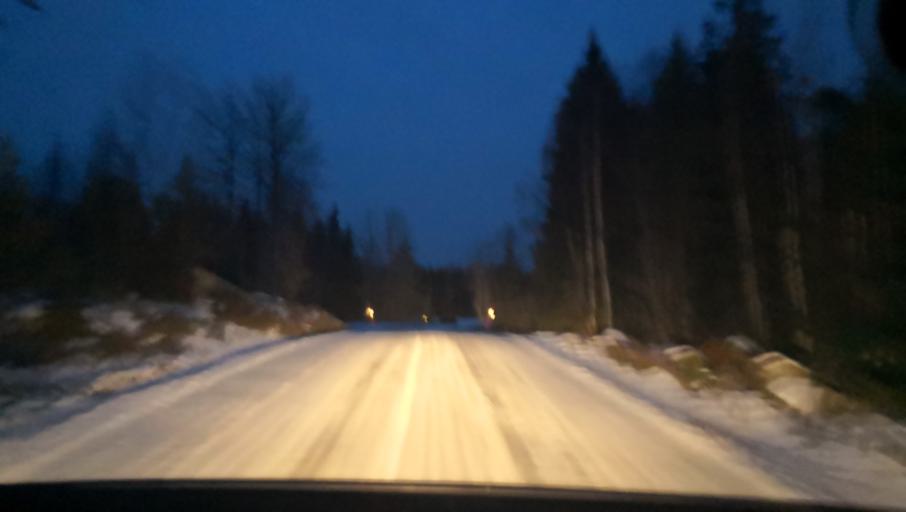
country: SE
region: Uppsala
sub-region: Heby Kommun
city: Tarnsjo
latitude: 60.2454
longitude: 16.7232
